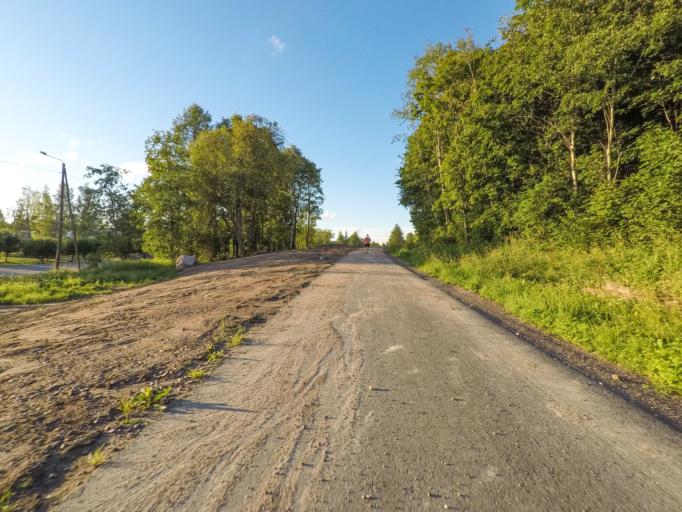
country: FI
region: South Karelia
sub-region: Imatra
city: Imatra
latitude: 61.1997
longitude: 28.7843
